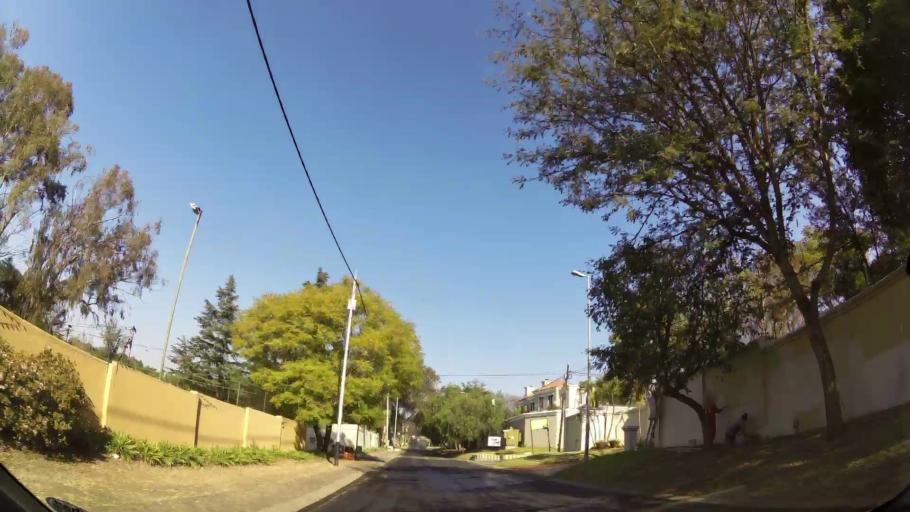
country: ZA
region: Gauteng
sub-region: City of Johannesburg Metropolitan Municipality
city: Diepsloot
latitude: -26.0685
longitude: 28.0081
